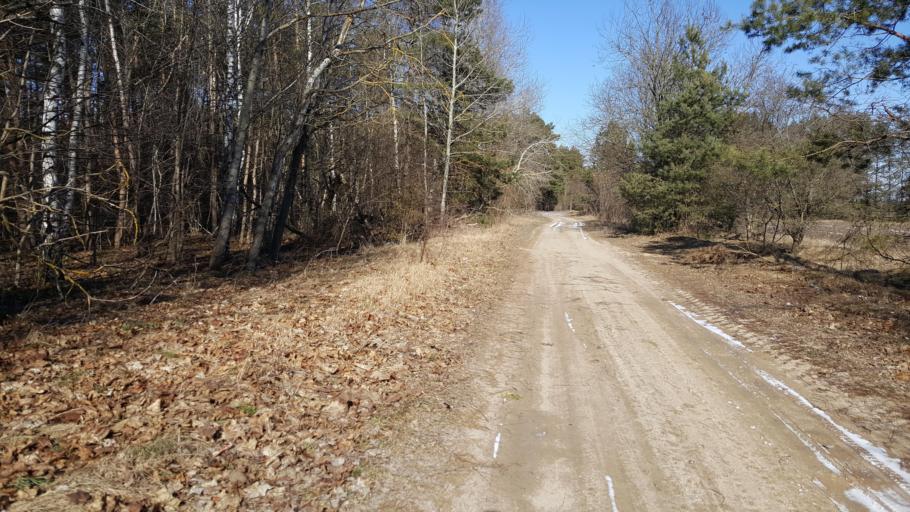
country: BY
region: Brest
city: Kamyanyets
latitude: 52.3859
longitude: 23.8455
